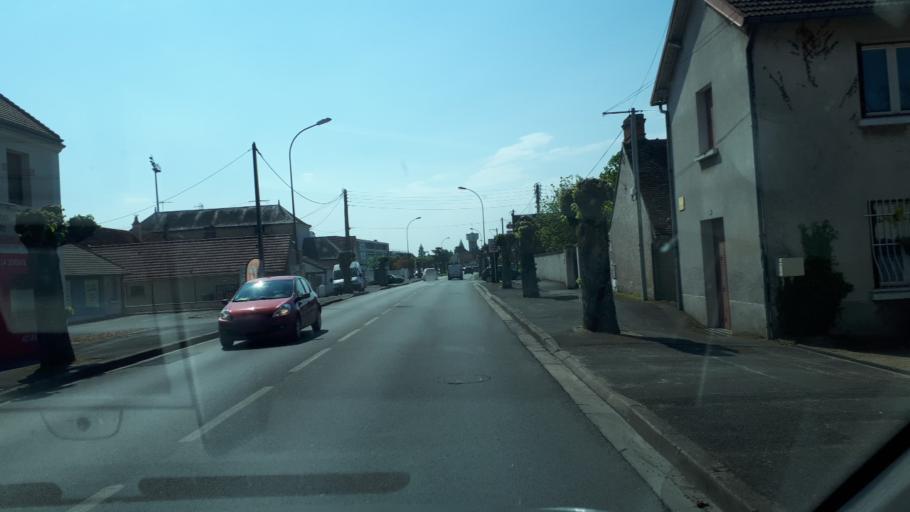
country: FR
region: Centre
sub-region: Departement du Loir-et-Cher
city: Romorantin-Lanthenay
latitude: 47.3711
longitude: 1.7383
